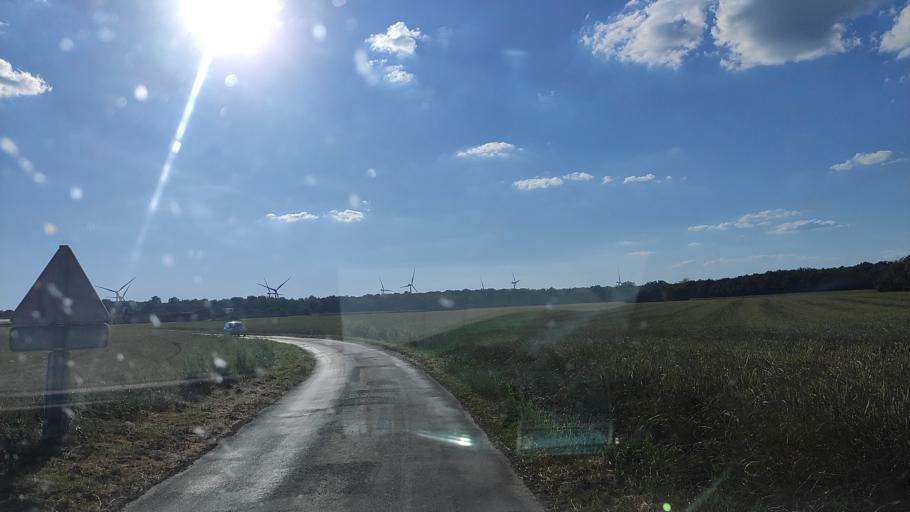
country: FR
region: Poitou-Charentes
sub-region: Departement des Deux-Sevres
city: Saint-Varent
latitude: 46.8587
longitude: -0.1922
